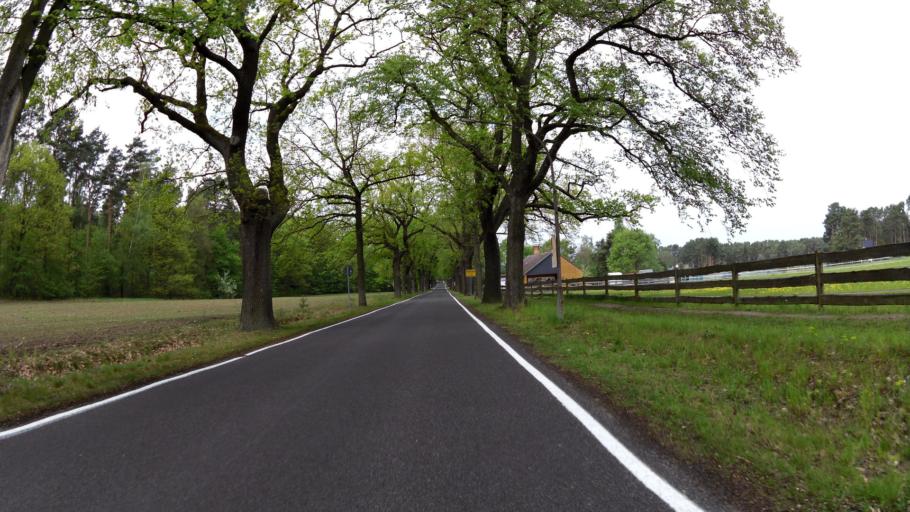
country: DE
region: Brandenburg
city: Mittenwalde
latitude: 52.2062
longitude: 13.5665
